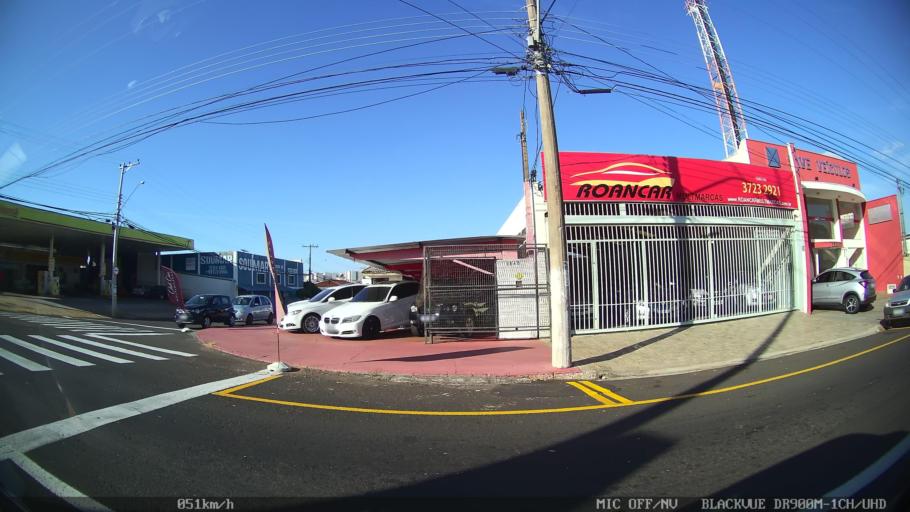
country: BR
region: Sao Paulo
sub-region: Franca
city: Franca
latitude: -20.5164
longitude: -47.3980
